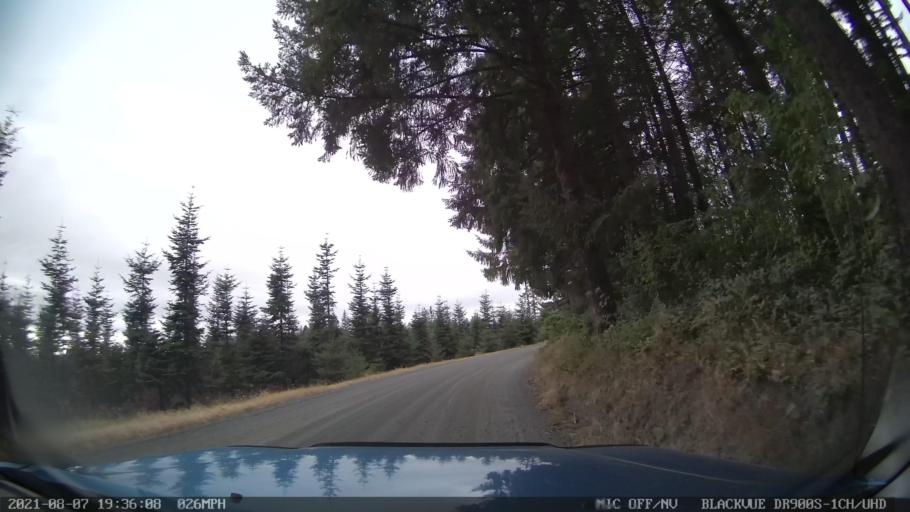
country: US
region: Oregon
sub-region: Marion County
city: Silverton
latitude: 44.9314
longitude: -122.6573
